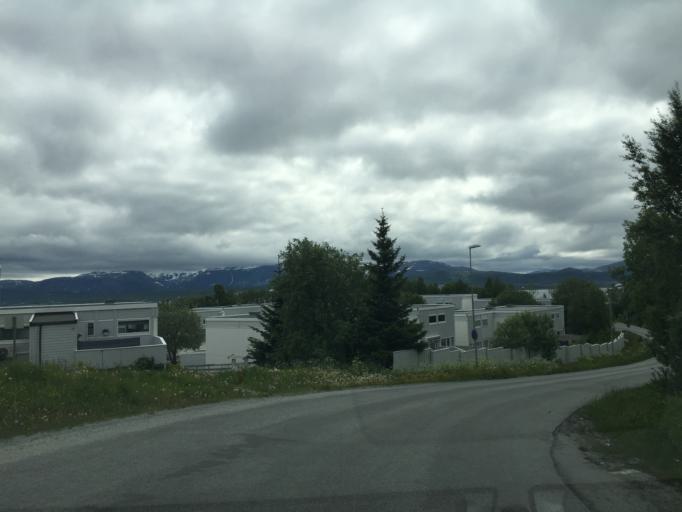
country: NO
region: Nordland
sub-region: Bodo
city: Lopsmarka
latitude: 67.2816
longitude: 14.5297
